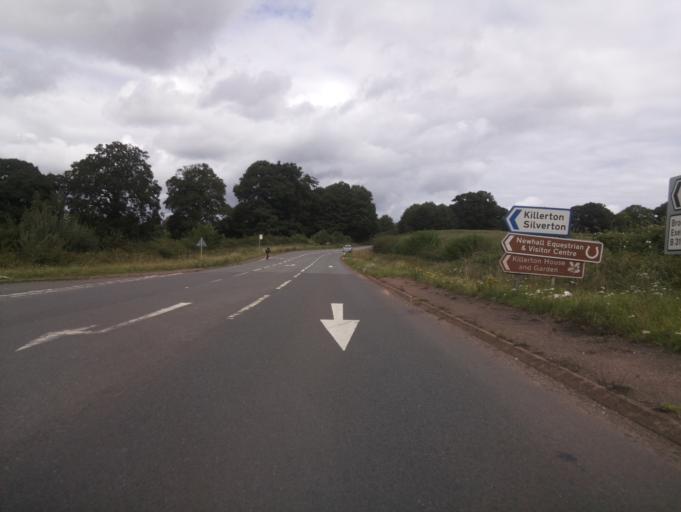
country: GB
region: England
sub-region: Devon
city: Bradninch
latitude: 50.7879
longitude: -3.4434
